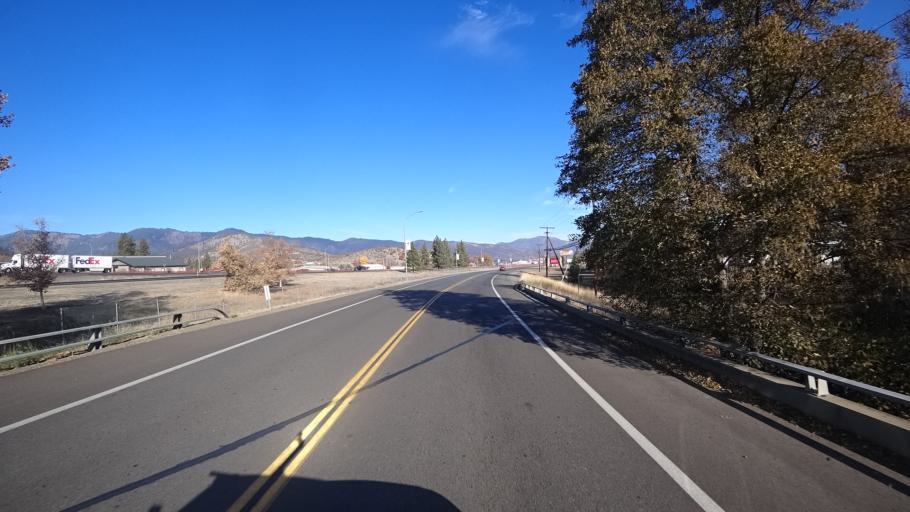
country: US
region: California
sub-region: Siskiyou County
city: Yreka
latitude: 41.7056
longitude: -122.6418
